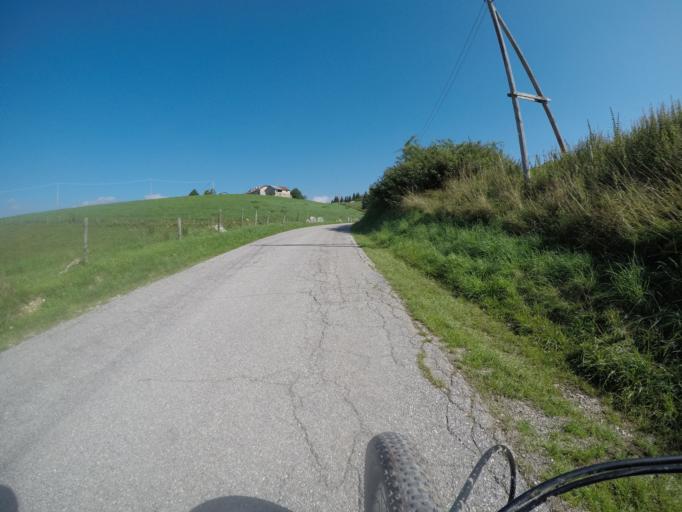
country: IT
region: Veneto
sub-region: Provincia di Vicenza
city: Canove di Roana
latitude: 45.8430
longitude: 11.4998
